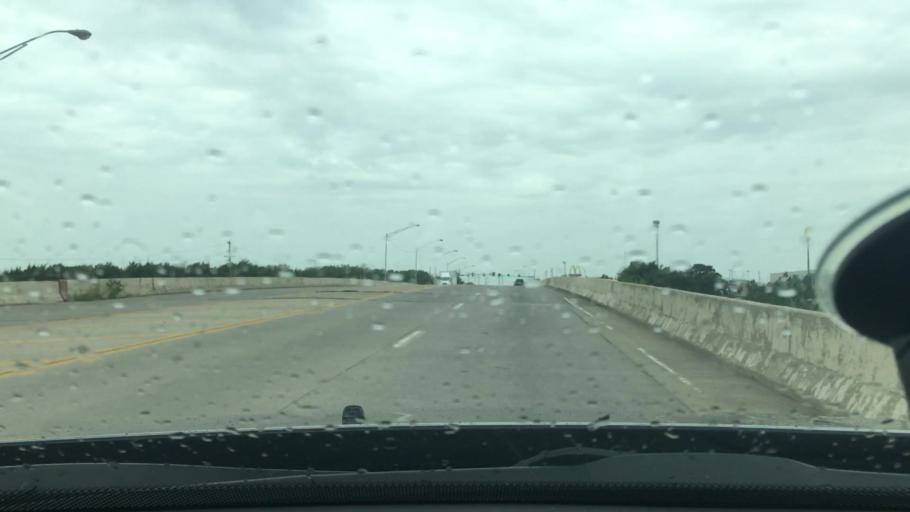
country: US
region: Oklahoma
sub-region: Carter County
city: Ardmore
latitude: 34.1875
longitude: -97.1655
